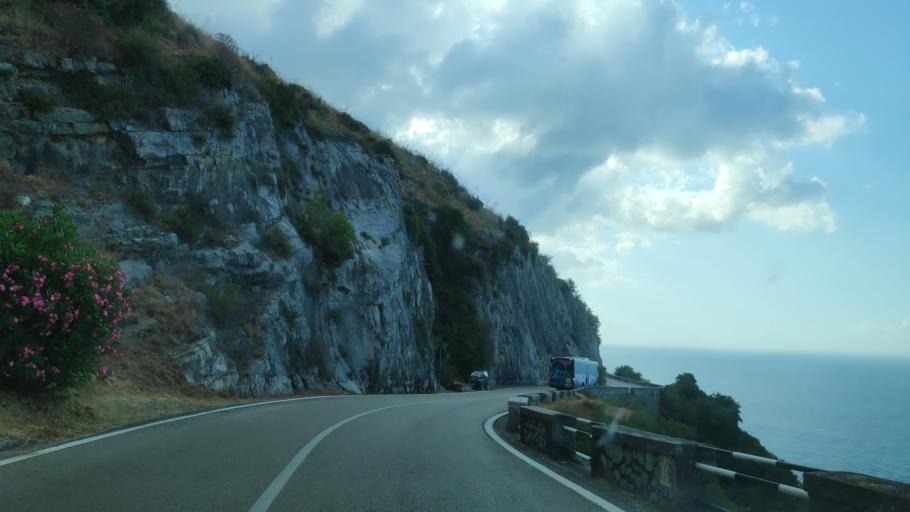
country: IT
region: Campania
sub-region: Provincia di Napoli
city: Arola-Preazzano
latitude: 40.6216
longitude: 14.4541
